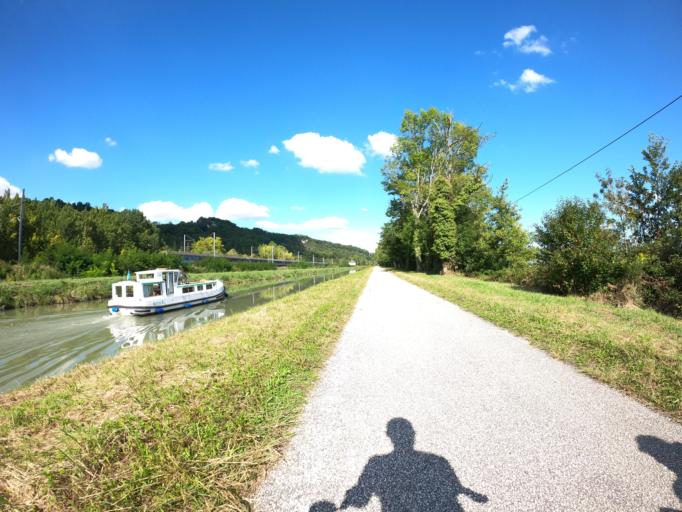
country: FR
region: Midi-Pyrenees
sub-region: Departement du Tarn-et-Garonne
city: Saint-Nicolas-de-la-Grave
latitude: 44.0867
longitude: 0.9881
